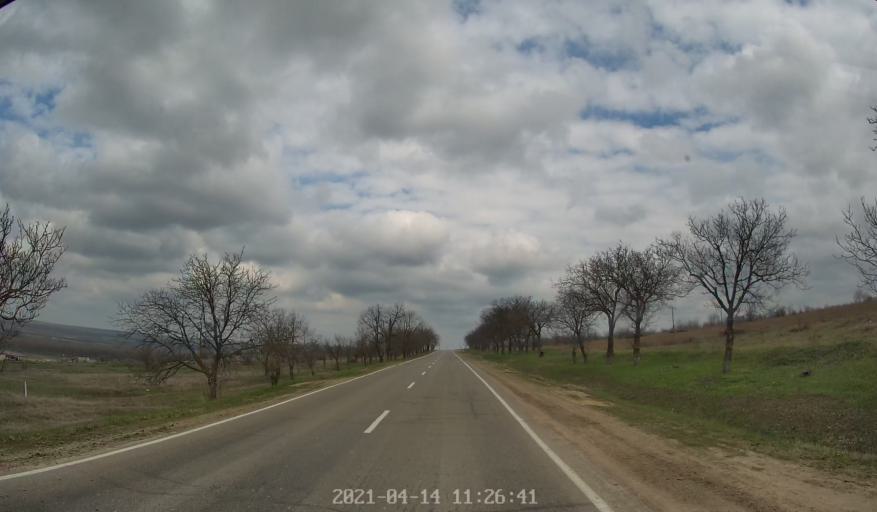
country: MD
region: Criuleni
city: Criuleni
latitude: 47.1663
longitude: 29.1633
